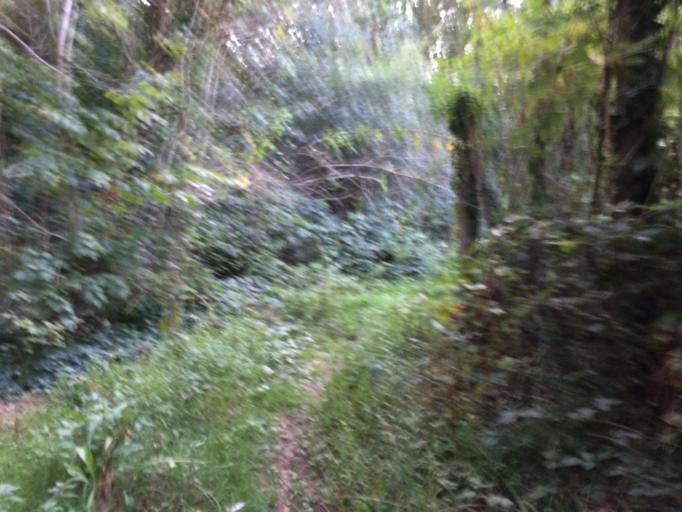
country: FR
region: Ile-de-France
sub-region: Departement de l'Essonne
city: Nozay
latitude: 48.6611
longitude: 2.2131
